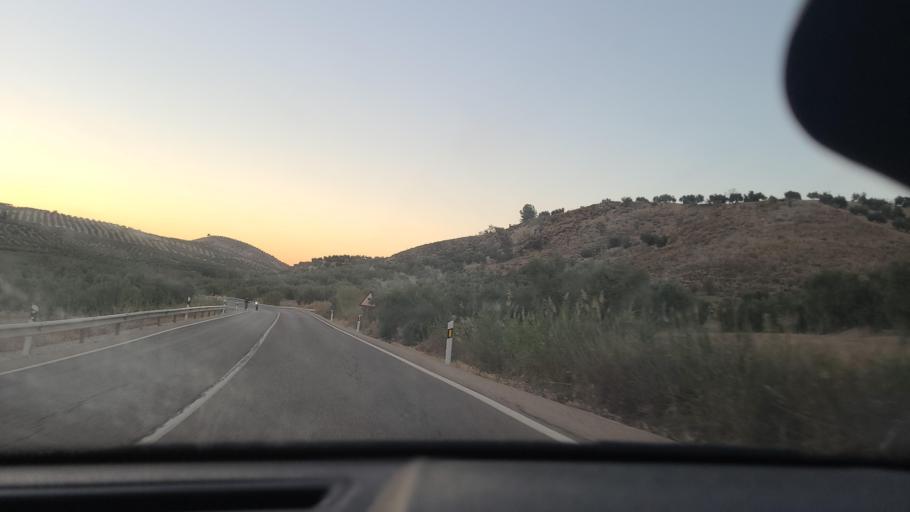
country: ES
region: Andalusia
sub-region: Provincia de Jaen
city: Jimena
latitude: 37.8257
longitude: -3.4329
